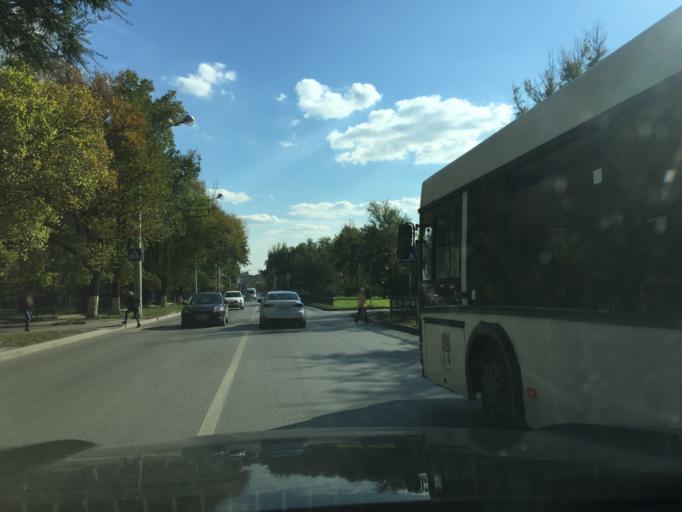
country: RU
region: Rostov
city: Rostov-na-Donu
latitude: 47.2109
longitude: 39.6455
